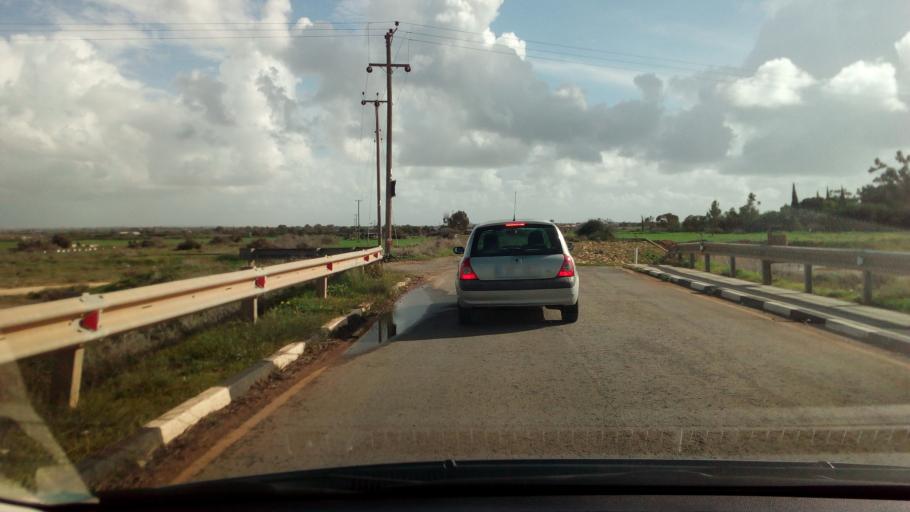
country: CY
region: Ammochostos
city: Avgorou
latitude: 35.0547
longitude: 33.8150
